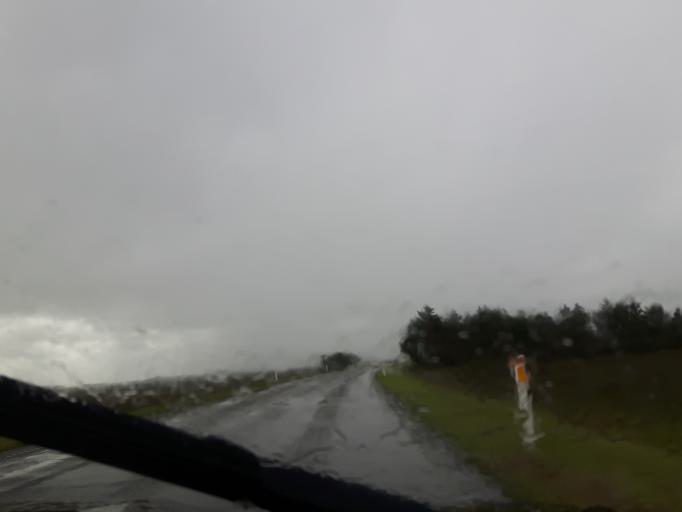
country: DK
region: North Denmark
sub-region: Thisted Kommune
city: Hanstholm
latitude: 57.0071
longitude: 8.4696
